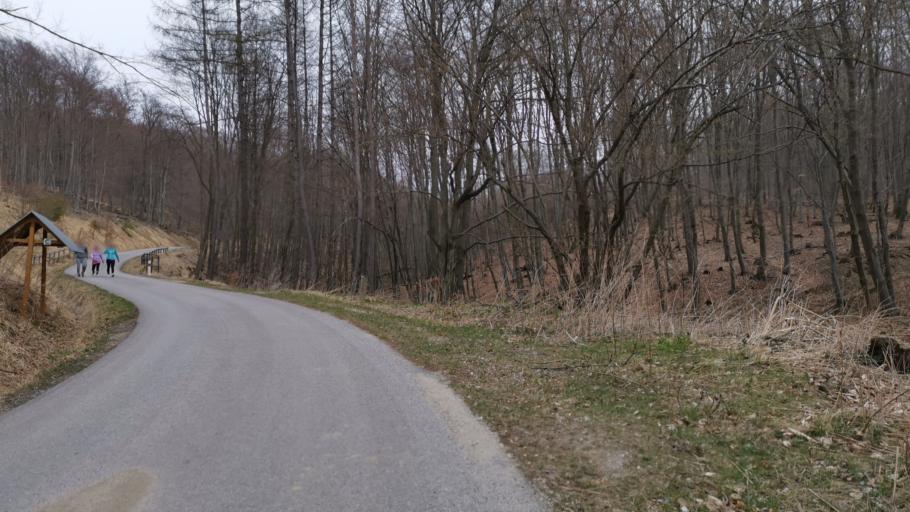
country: CZ
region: South Moravian
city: Petrov
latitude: 48.8153
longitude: 17.3344
